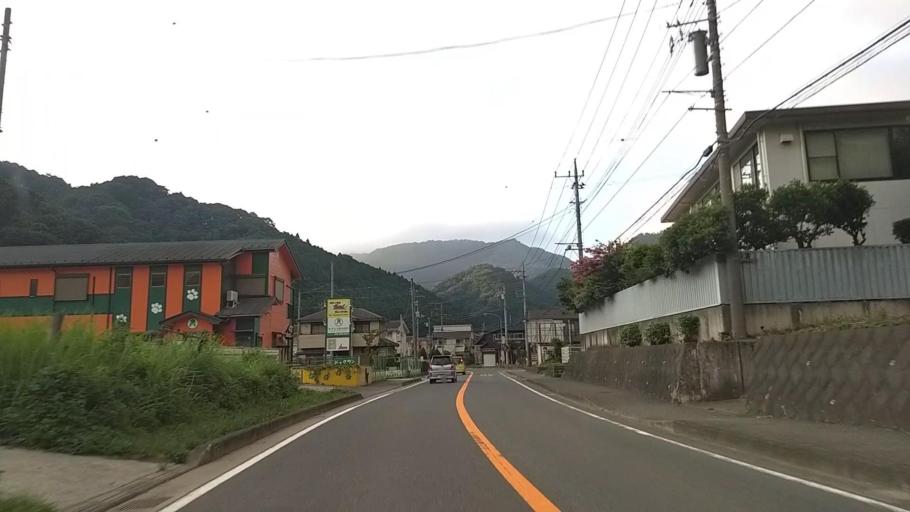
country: JP
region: Kanagawa
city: Atsugi
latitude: 35.4753
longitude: 139.2940
